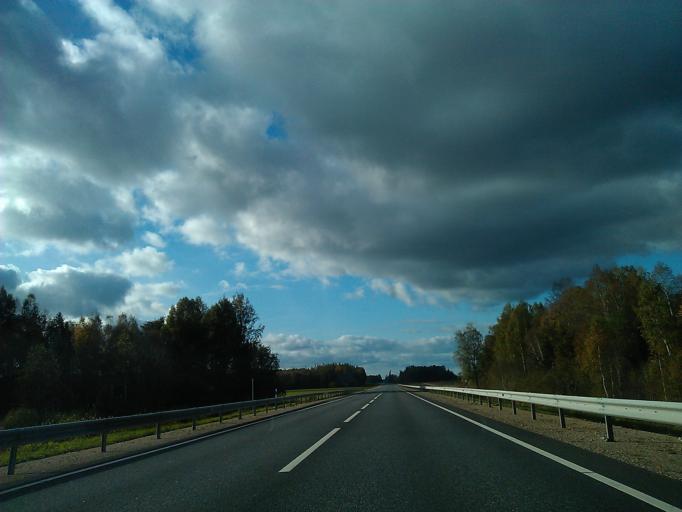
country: LV
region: Ogre
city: Jumprava
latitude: 56.7850
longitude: 25.0079
